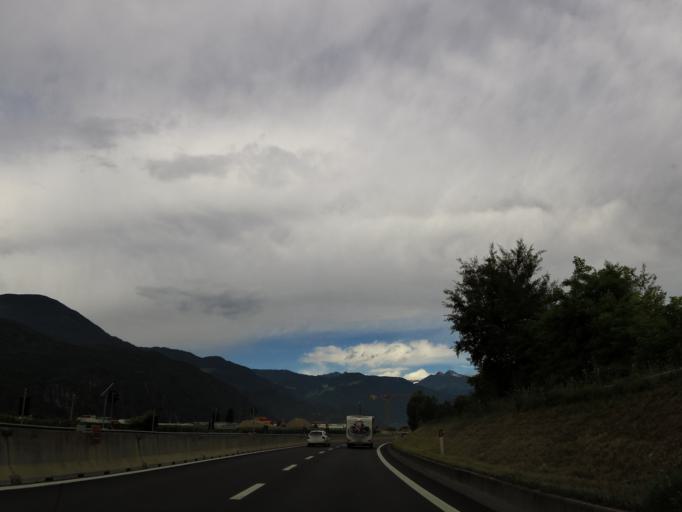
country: IT
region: Trentino-Alto Adige
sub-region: Bolzano
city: Nalles
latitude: 46.5511
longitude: 11.2204
